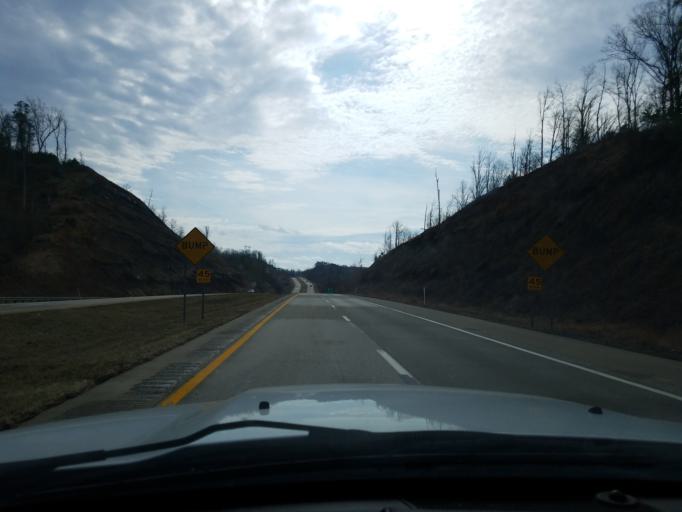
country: US
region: West Virginia
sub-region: Putnam County
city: Eleanor
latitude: 38.5184
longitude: -81.9327
